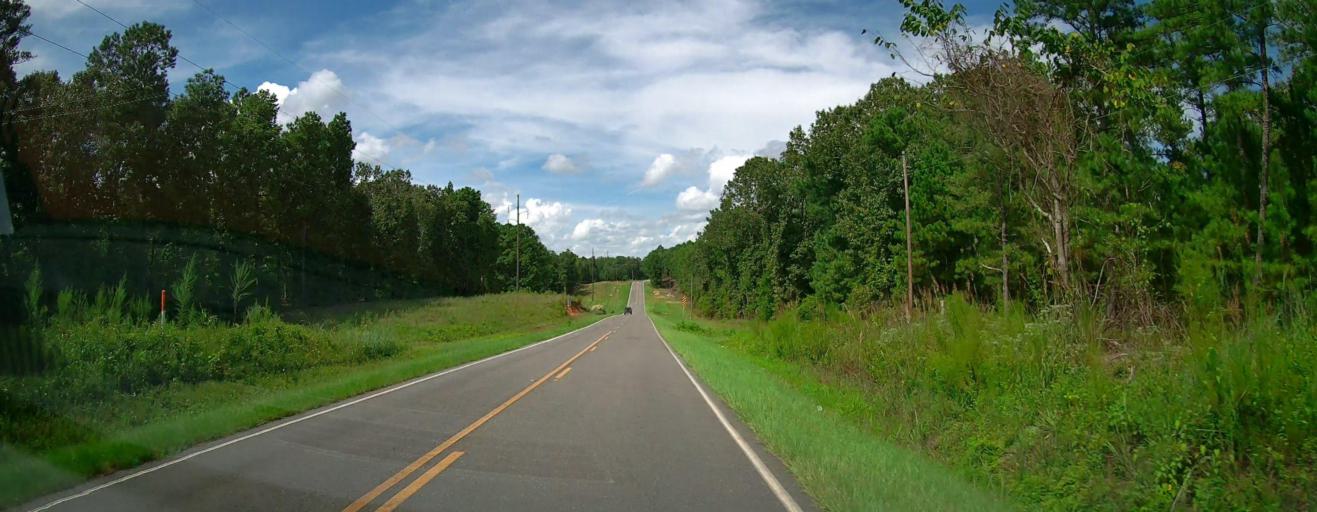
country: US
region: Georgia
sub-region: Taylor County
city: Butler
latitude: 32.5092
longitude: -84.2037
